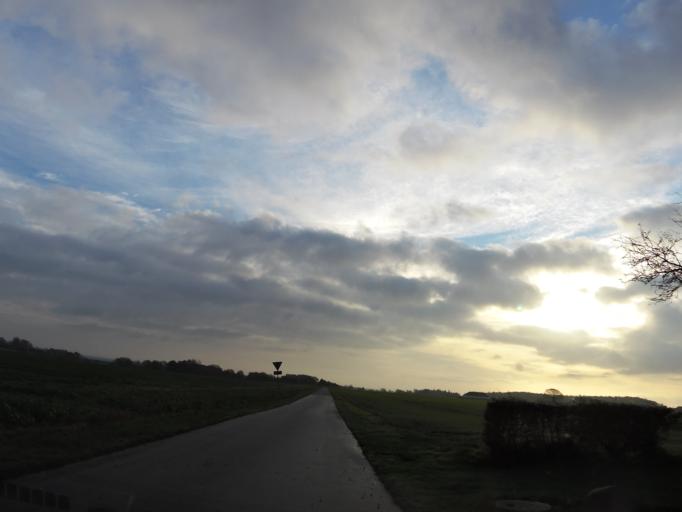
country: DK
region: Central Jutland
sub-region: Odder Kommune
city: Odder
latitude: 55.9303
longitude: 10.2394
